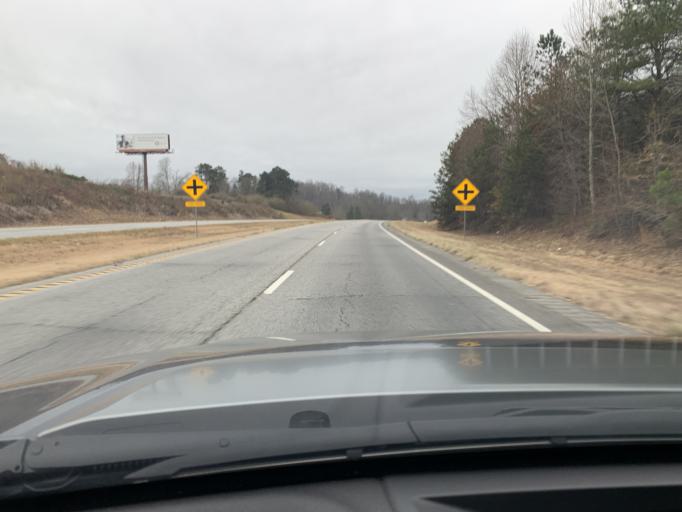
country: US
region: Georgia
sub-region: Habersham County
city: Mount Airy
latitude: 34.5788
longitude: -83.4597
